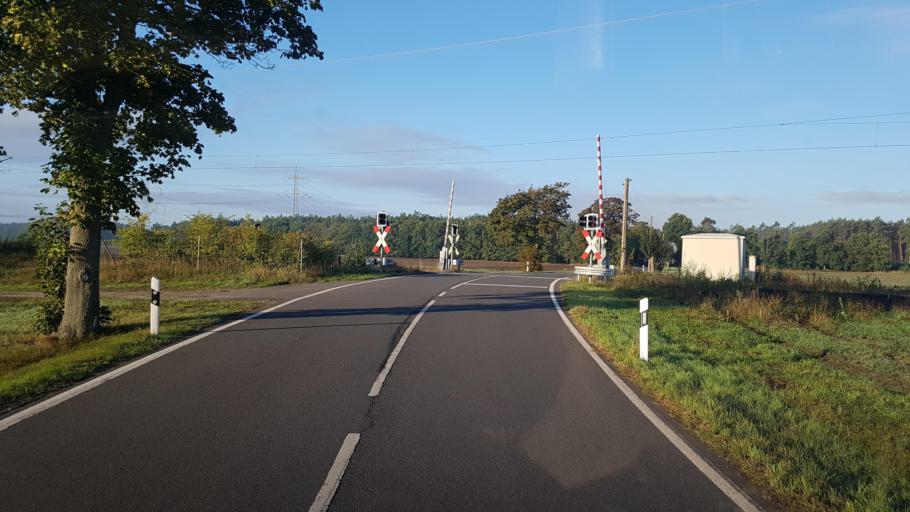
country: DE
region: Saxony-Anhalt
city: Holzdorf
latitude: 51.8204
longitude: 13.0989
